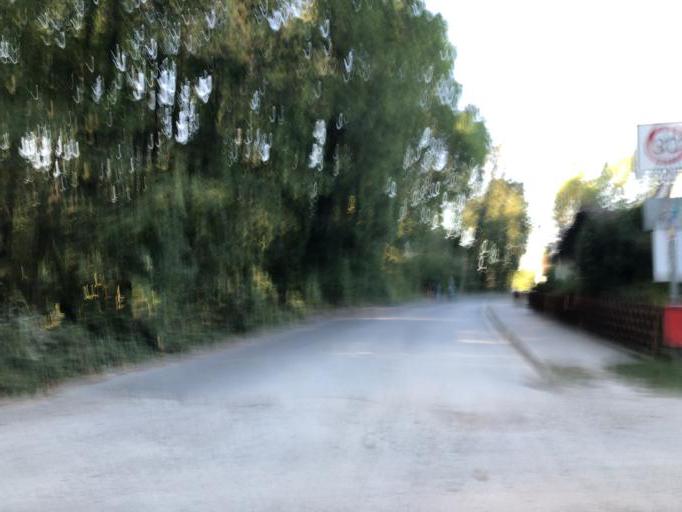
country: DE
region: Bavaria
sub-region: Regierungsbezirk Mittelfranken
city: Buckenhof
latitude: 49.5881
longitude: 11.0486
